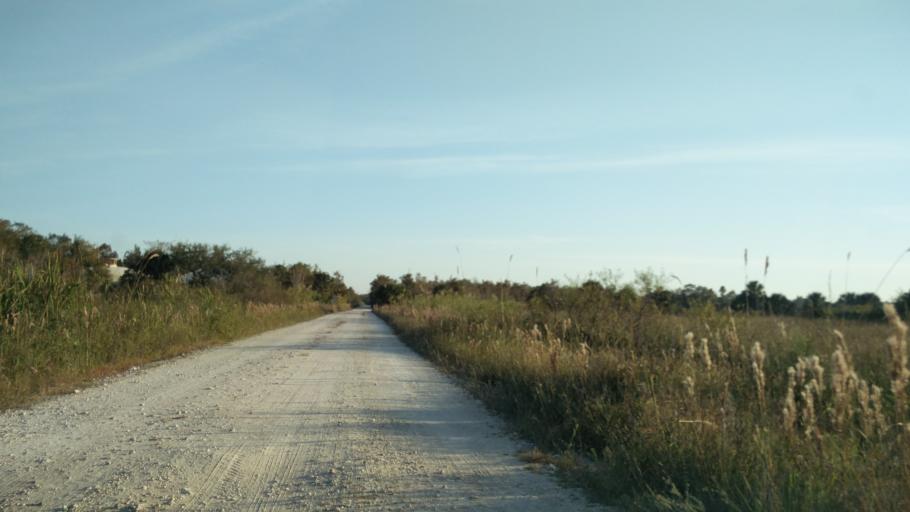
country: US
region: Florida
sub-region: Collier County
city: Lely Resort
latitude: 25.9585
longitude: -81.3633
